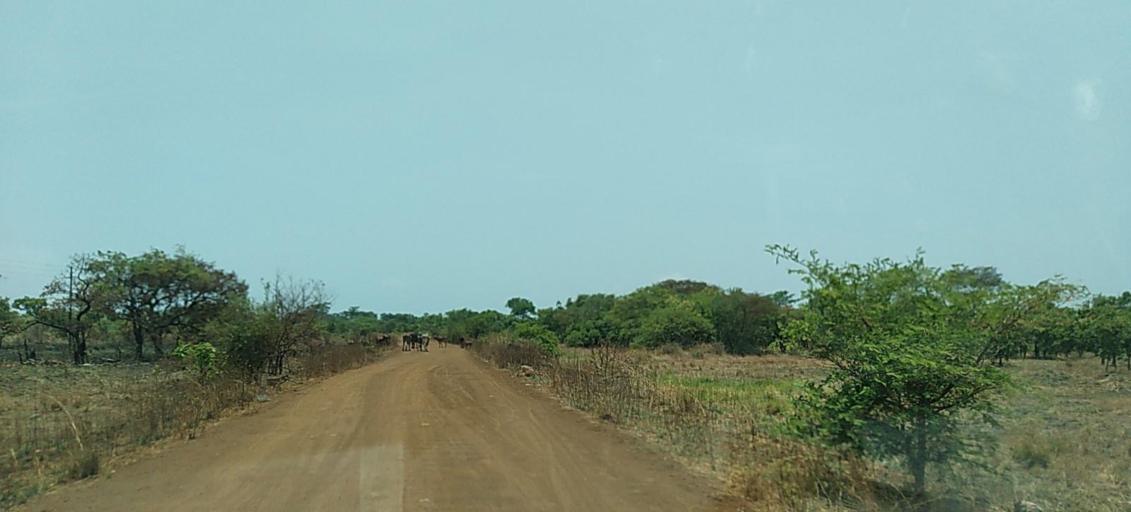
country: ZM
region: Copperbelt
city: Mpongwe
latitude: -13.7022
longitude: 27.8678
